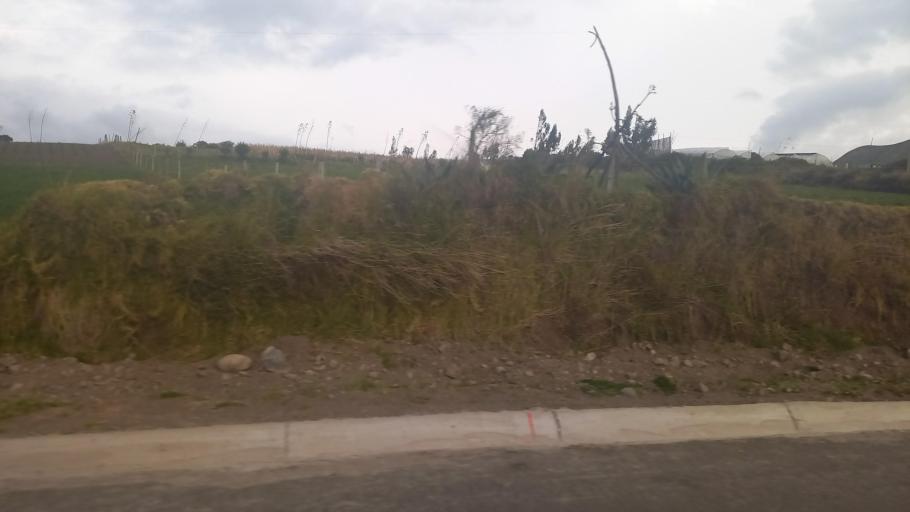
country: EC
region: Pichincha
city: Cayambe
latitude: 0.1326
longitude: -78.0679
